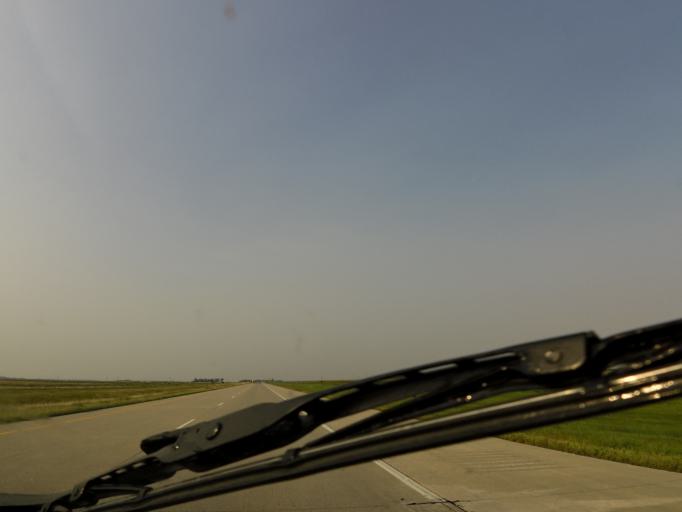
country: US
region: North Dakota
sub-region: Cass County
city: Horace
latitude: 46.6045
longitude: -96.8233
